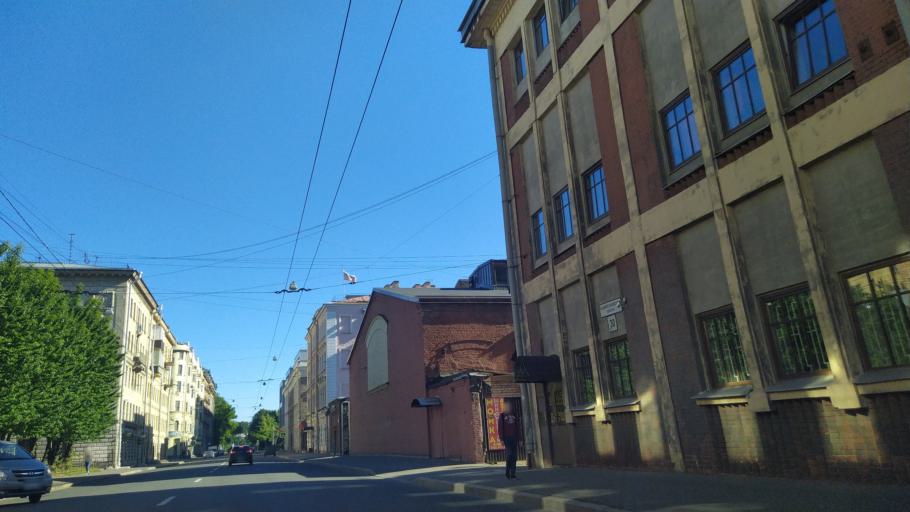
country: RU
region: Leningrad
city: Sampsonievskiy
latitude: 59.9659
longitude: 30.3431
